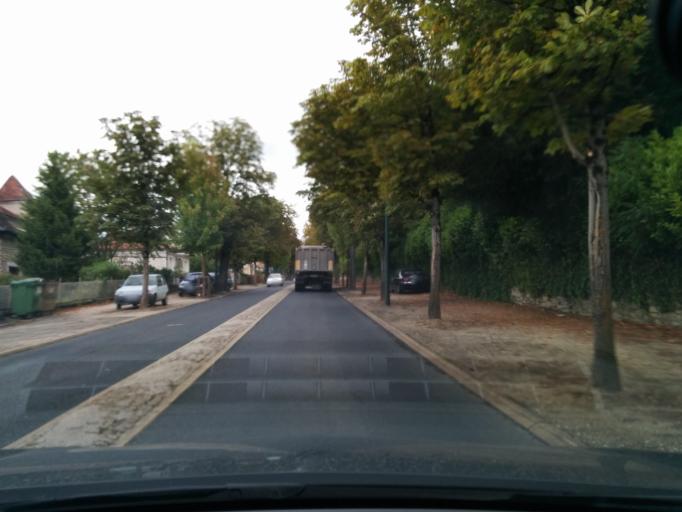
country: FR
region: Midi-Pyrenees
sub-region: Departement du Lot
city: Souillac
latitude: 44.8883
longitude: 1.4831
